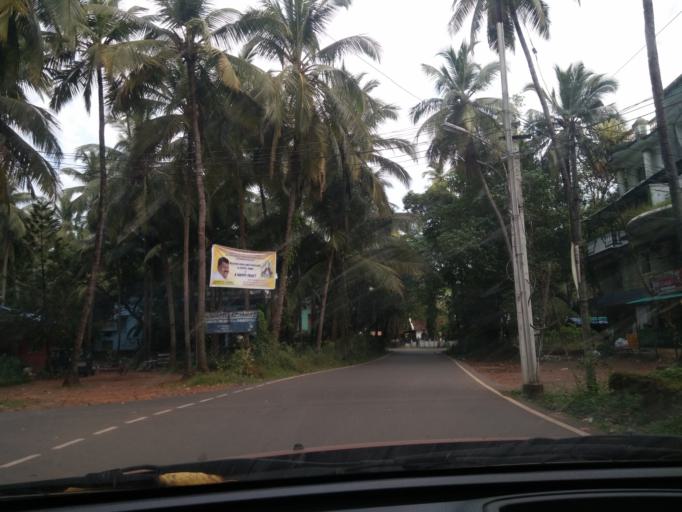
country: IN
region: Goa
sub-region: South Goa
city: Benaulim
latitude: 15.2676
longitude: 73.9287
